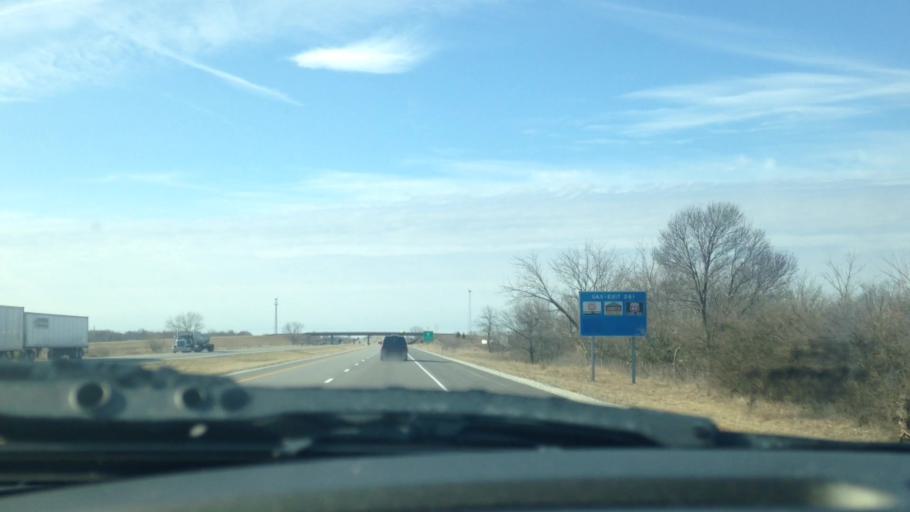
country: US
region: Illinois
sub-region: Ford County
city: Paxton
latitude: 40.4784
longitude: -88.1020
